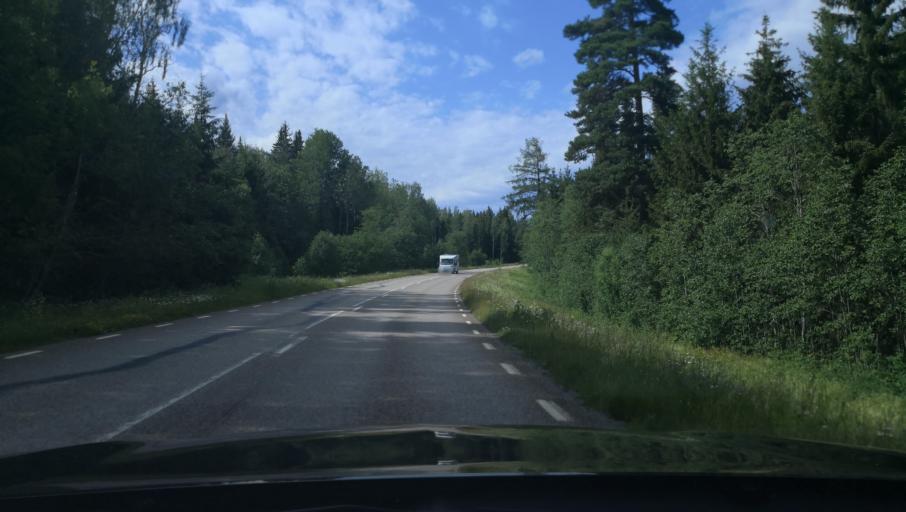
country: SE
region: Dalarna
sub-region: Avesta Kommun
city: Avesta
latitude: 59.9738
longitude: 16.1496
